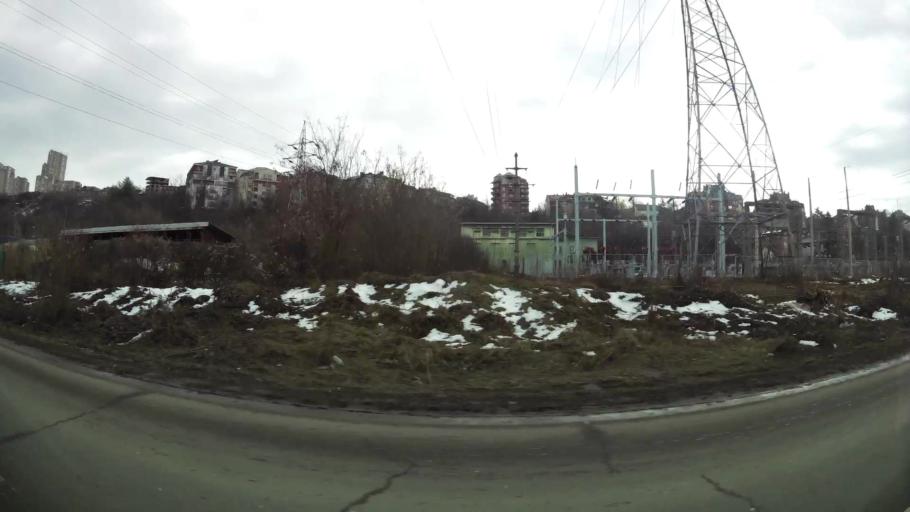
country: RS
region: Central Serbia
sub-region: Belgrade
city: Cukarica
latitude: 44.7652
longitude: 20.4058
